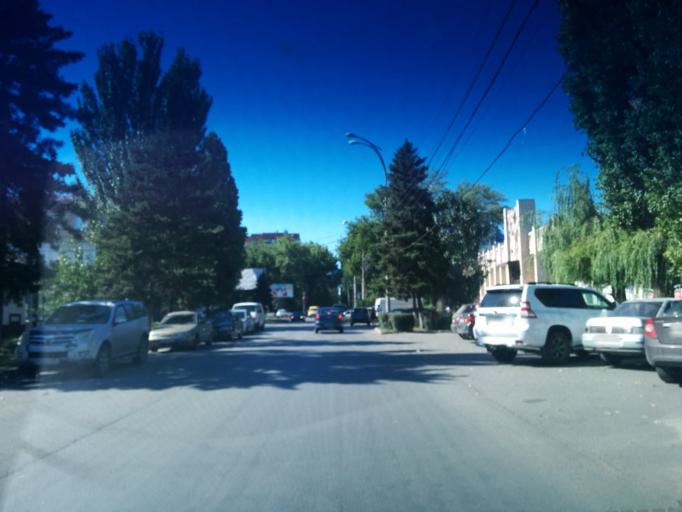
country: RU
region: Rostov
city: Shakhty
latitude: 47.7095
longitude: 40.2190
